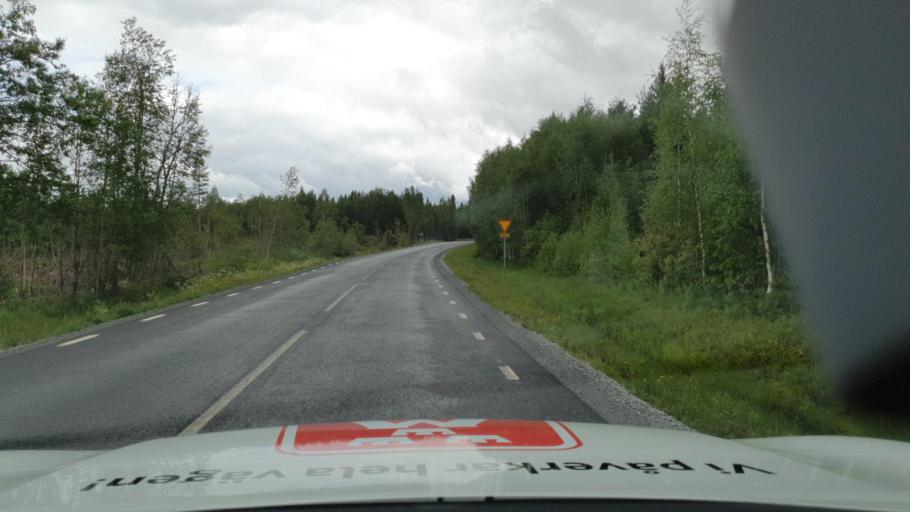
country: SE
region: Vaesterbotten
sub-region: Dorotea Kommun
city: Dorotea
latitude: 64.2472
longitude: 16.5319
